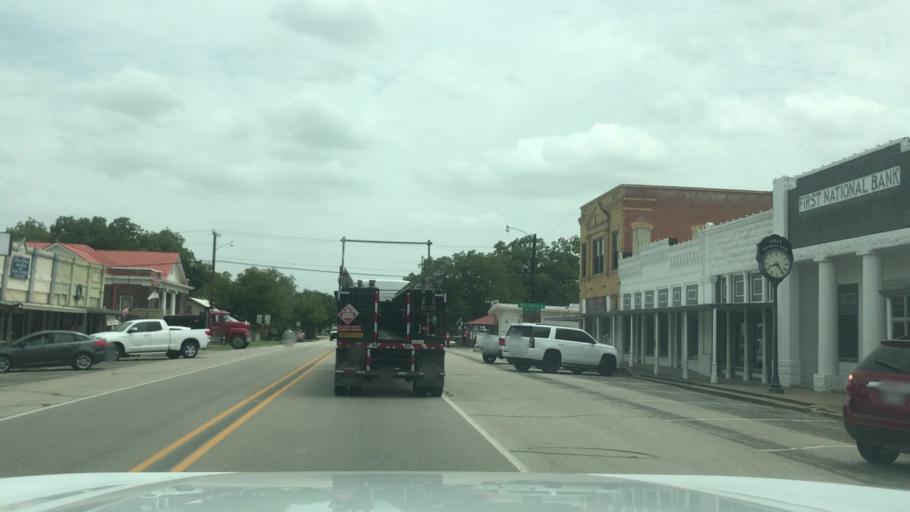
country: US
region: Texas
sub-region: Bosque County
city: Valley Mills
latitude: 31.6590
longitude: -97.4720
